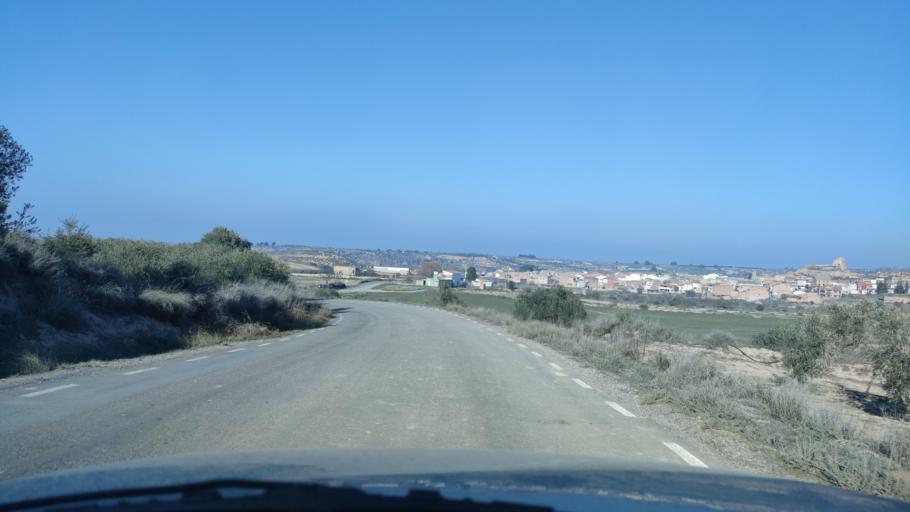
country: ES
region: Catalonia
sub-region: Provincia de Lleida
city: Torrebesses
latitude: 41.4531
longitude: 0.5579
